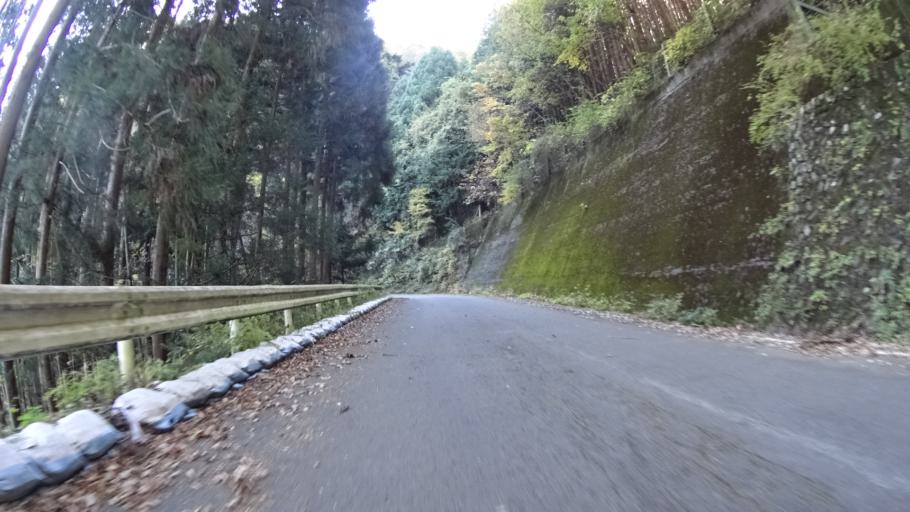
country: JP
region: Yamanashi
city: Otsuki
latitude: 35.7436
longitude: 138.9601
